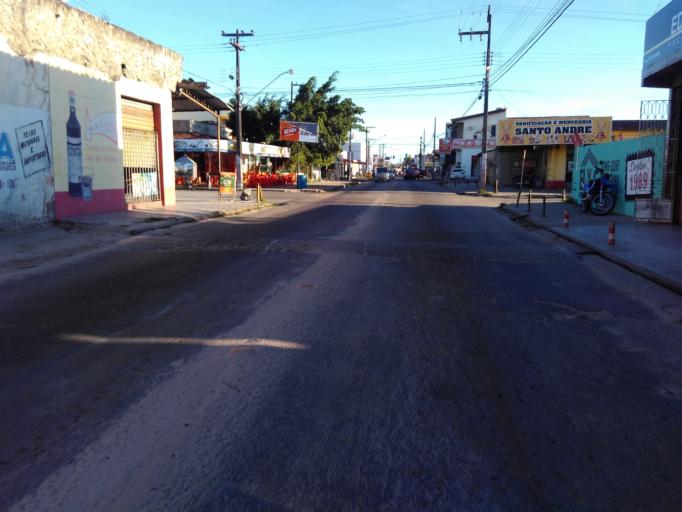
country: BR
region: Sergipe
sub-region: Aracaju
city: Aracaju
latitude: -10.8905
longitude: -37.0848
